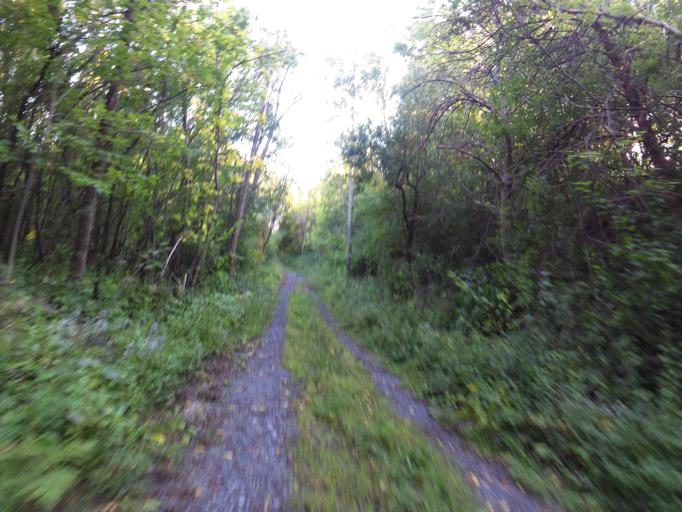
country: CA
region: Quebec
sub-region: Outaouais
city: Gatineau
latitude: 45.4579
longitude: -75.7261
